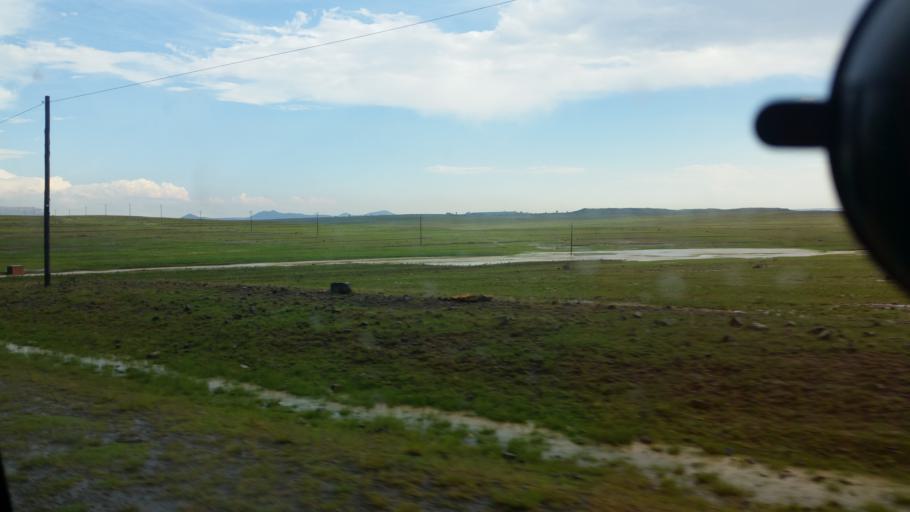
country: LS
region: Mafeteng
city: Mafeteng
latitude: -29.7749
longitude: 27.1919
